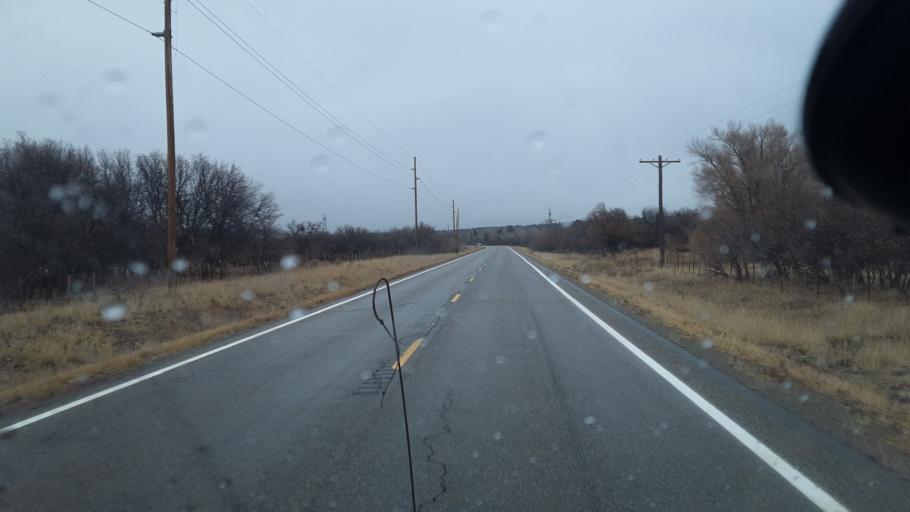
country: US
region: Colorado
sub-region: La Plata County
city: Durango
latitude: 37.2371
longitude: -108.0425
